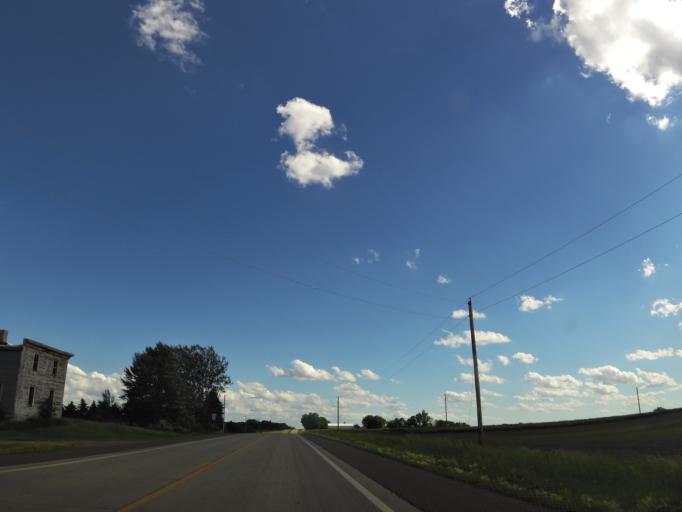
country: US
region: Minnesota
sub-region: Wright County
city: Cokato
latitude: 44.9806
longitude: -94.1750
